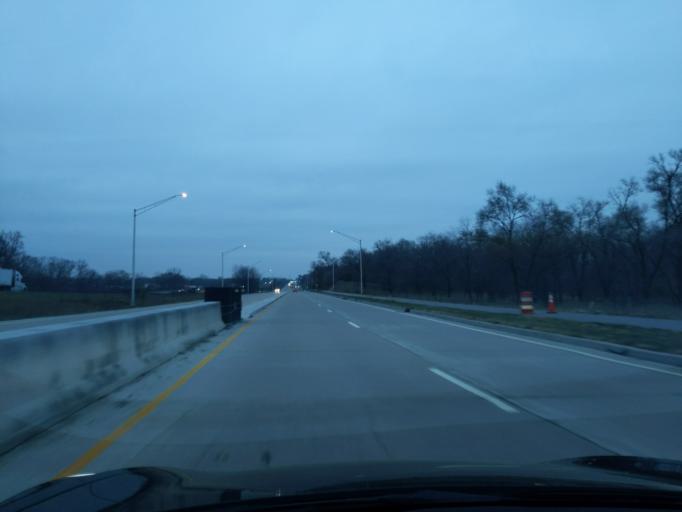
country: US
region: Indiana
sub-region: Saint Joseph County
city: Notre Dame
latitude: 41.7232
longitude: -86.2625
